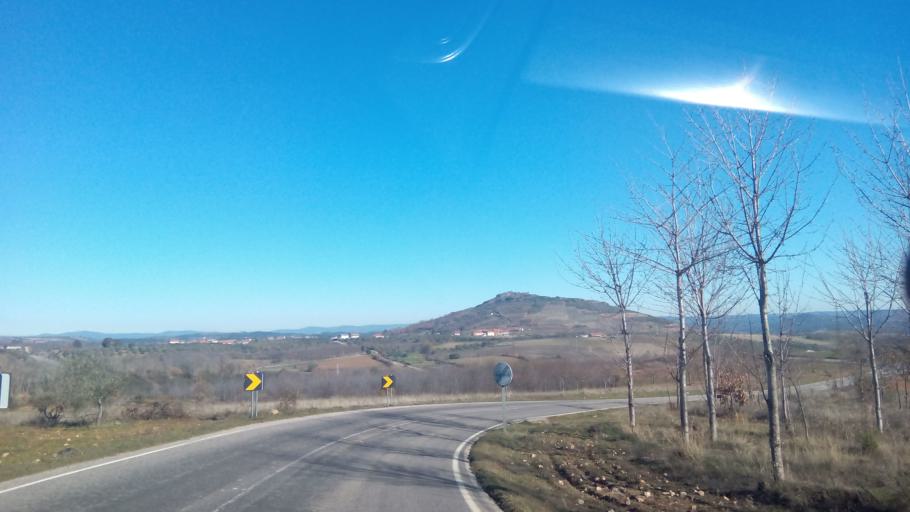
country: PT
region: Braganca
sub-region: Vimioso
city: Vimioso
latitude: 41.6729
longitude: -6.6102
